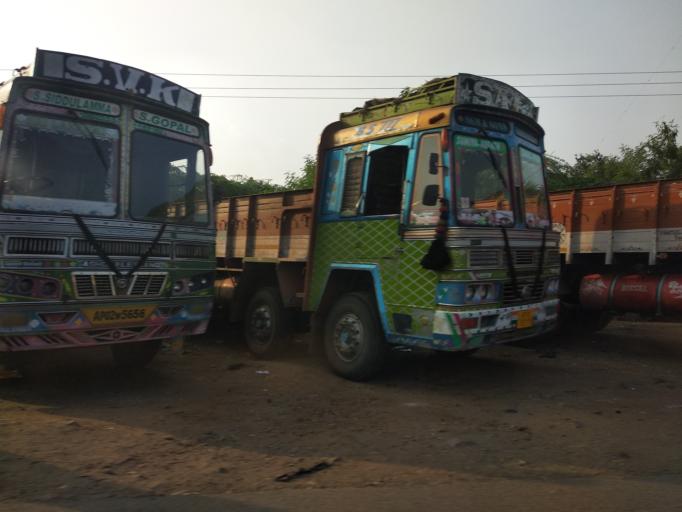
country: IN
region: Andhra Pradesh
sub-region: Vishakhapatnam
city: Visakhapatnam
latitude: 17.6846
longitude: 83.1626
